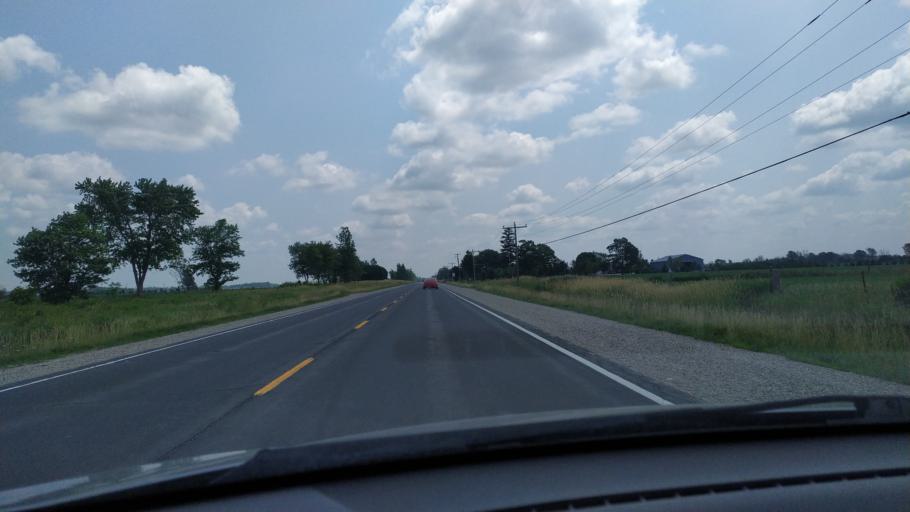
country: CA
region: Ontario
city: Stratford
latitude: 43.3700
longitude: -80.8851
